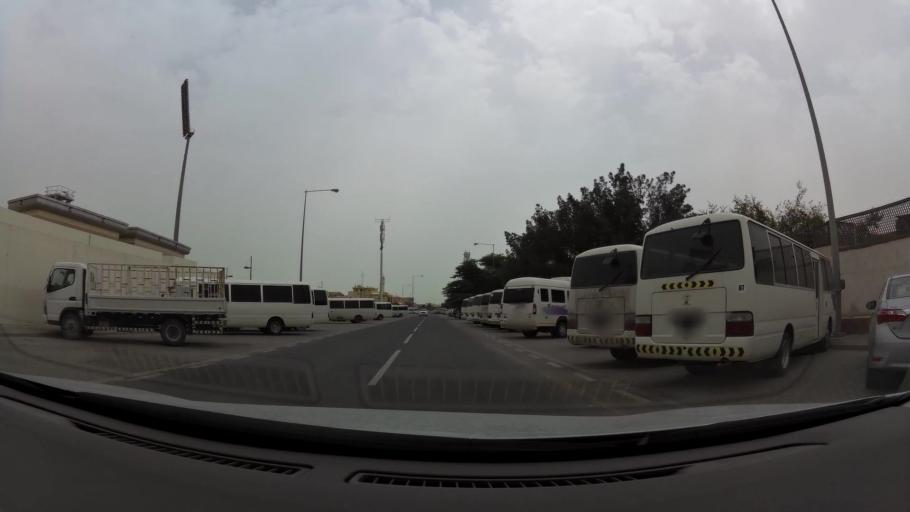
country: QA
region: Baladiyat ad Dawhah
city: Doha
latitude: 25.2573
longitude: 51.5203
